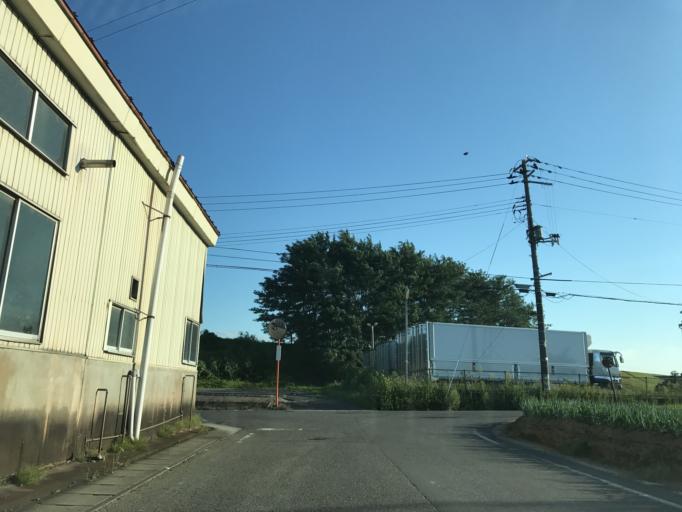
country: JP
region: Fukushima
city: Koriyama
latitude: 37.4058
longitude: 140.4032
